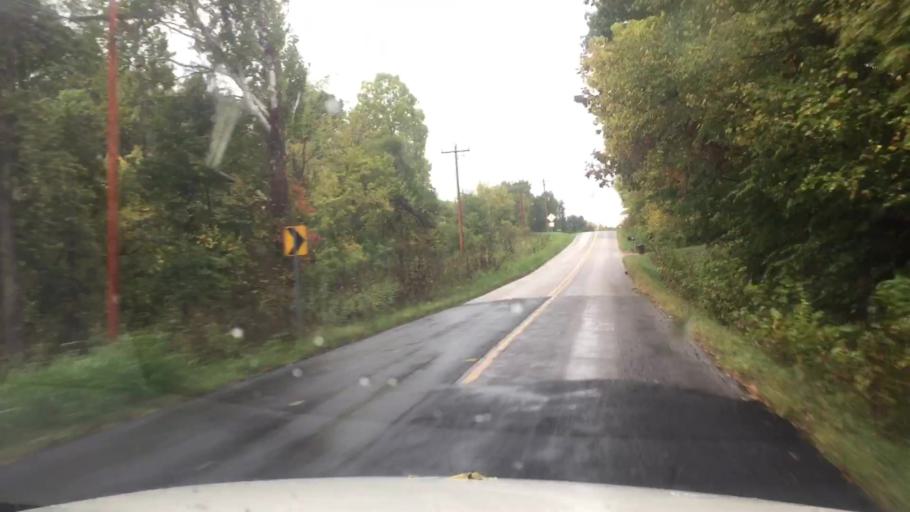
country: US
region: Missouri
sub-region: Boone County
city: Columbia
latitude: 38.9326
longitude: -92.4904
